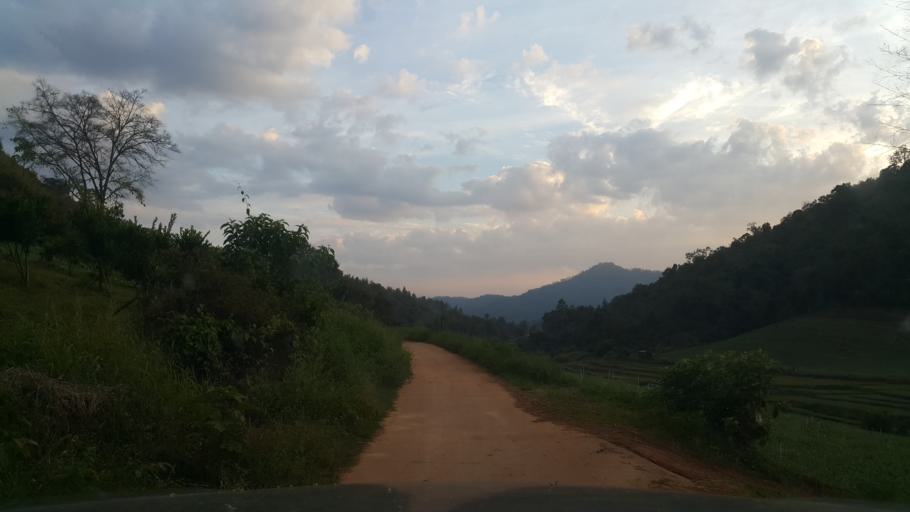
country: TH
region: Chiang Mai
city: Samoeng
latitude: 18.9711
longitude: 98.6803
